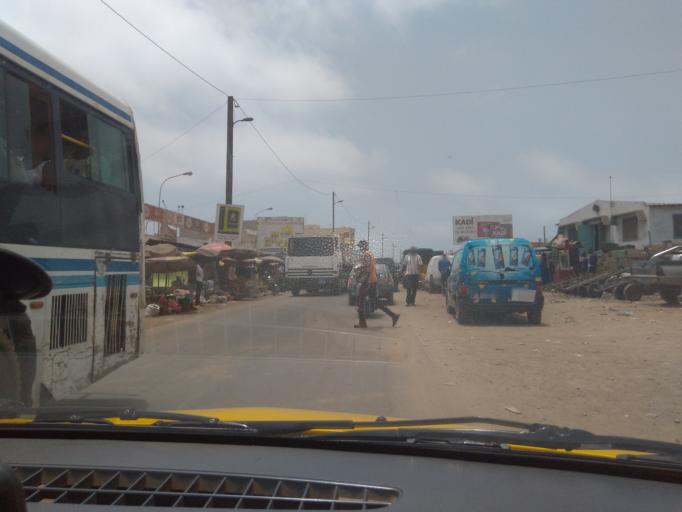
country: SN
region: Dakar
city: Pikine
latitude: 14.7537
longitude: -17.4288
